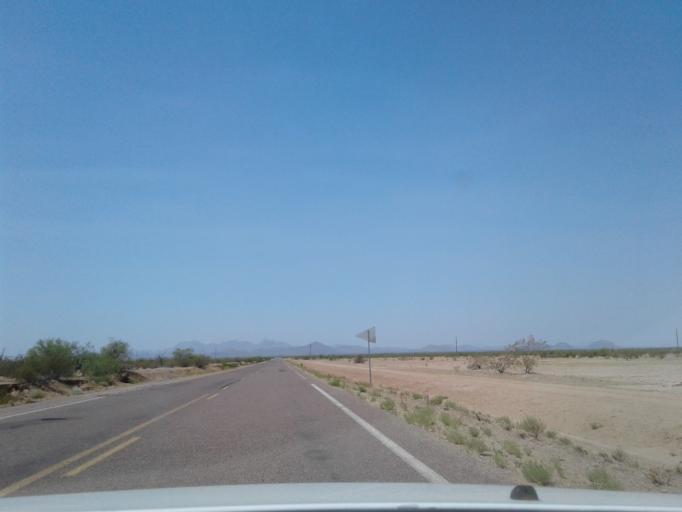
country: US
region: Arizona
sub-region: Pima County
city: Avra Valley
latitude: 32.6092
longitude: -111.3180
